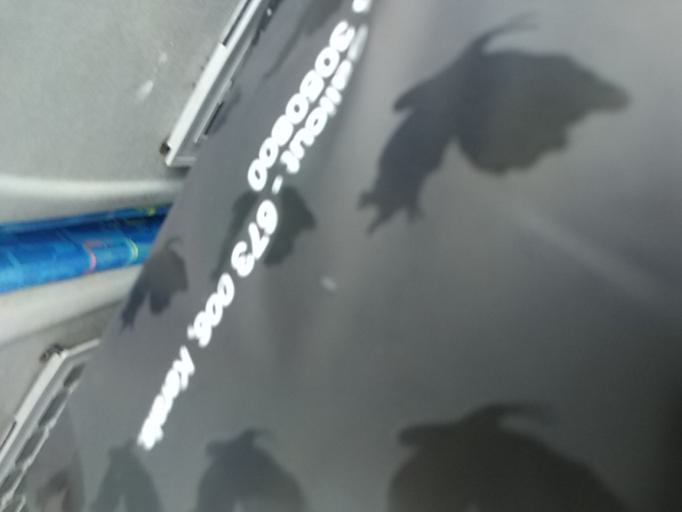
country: IN
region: Kerala
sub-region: Kozhikode
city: Kozhikode
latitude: 11.2887
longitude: 75.7665
